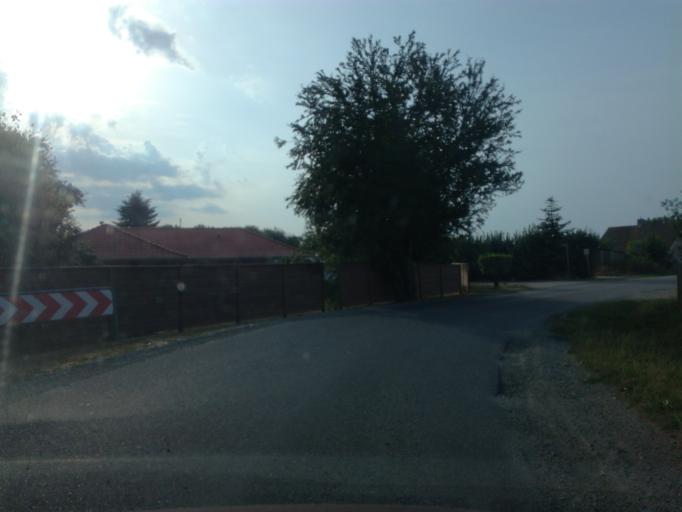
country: DK
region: South Denmark
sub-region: Vejle Kommune
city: Borkop
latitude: 55.6415
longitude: 9.5959
